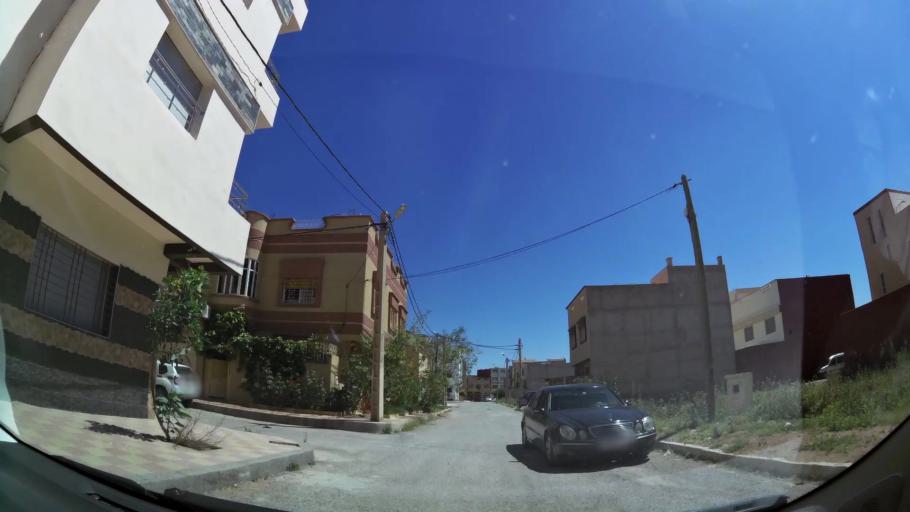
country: MA
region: Oriental
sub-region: Oujda-Angad
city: Oujda
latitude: 34.6715
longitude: -1.8685
